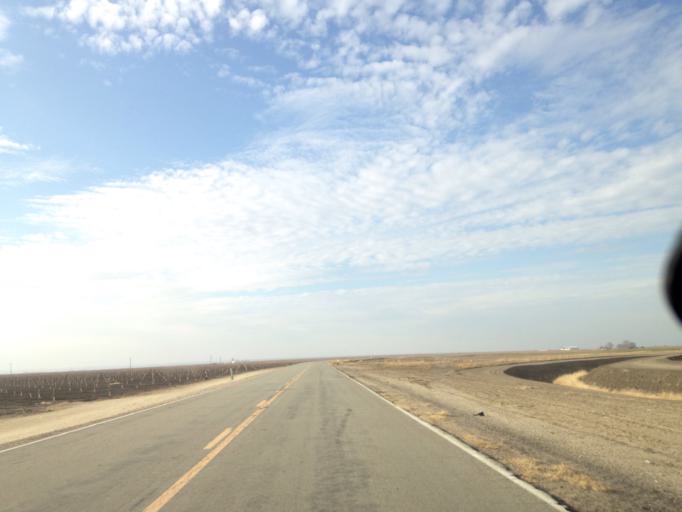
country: US
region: California
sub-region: Kern County
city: Buttonwillow
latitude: 35.4460
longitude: -119.5559
